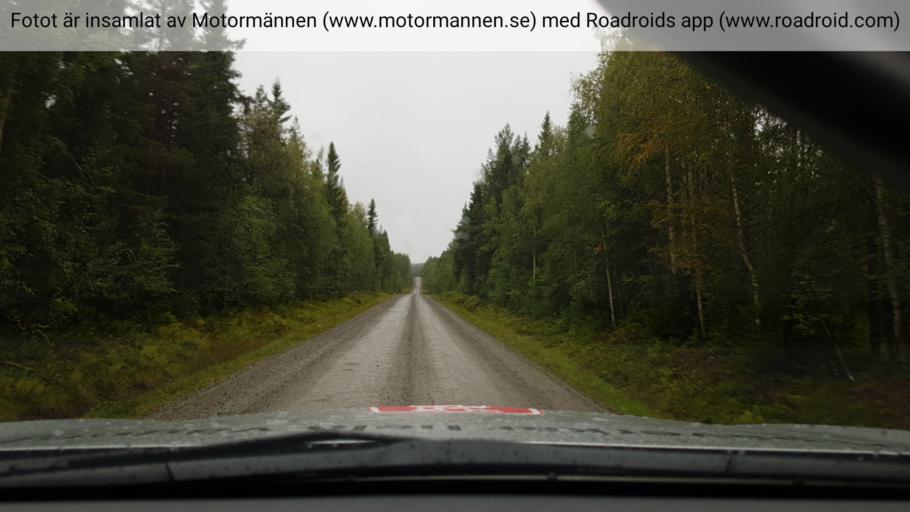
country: SE
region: Vaesterbotten
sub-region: Asele Kommun
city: Asele
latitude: 64.0076
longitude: 17.6146
